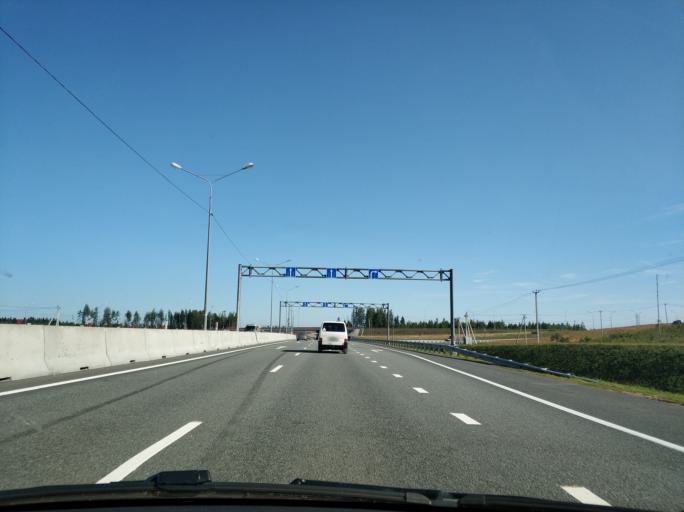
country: RU
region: Leningrad
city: Sosnovo
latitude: 60.4992
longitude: 30.1957
